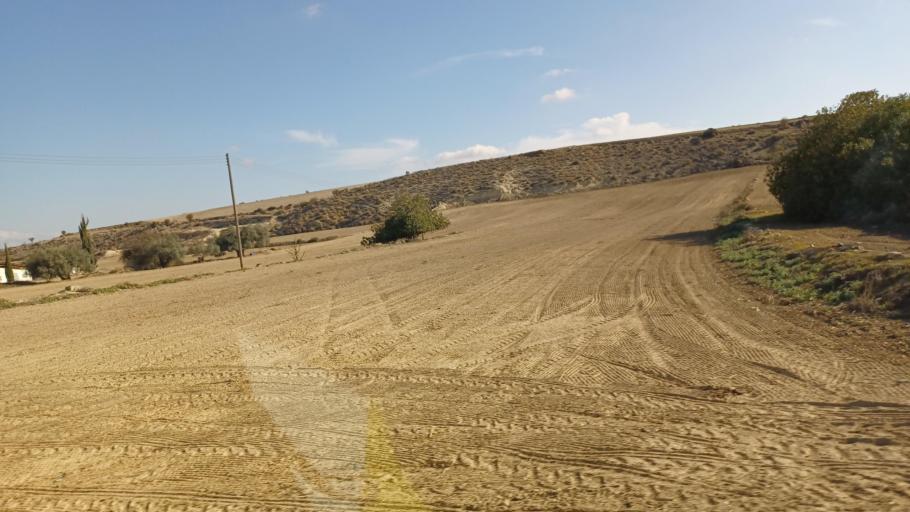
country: CY
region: Larnaka
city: Athienou
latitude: 35.0426
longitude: 33.5559
